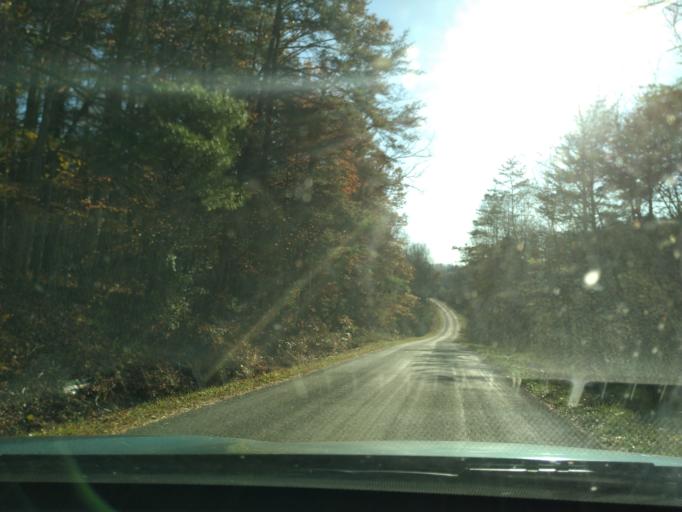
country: US
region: Virginia
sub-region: Floyd County
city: Floyd
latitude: 36.8263
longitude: -80.2107
